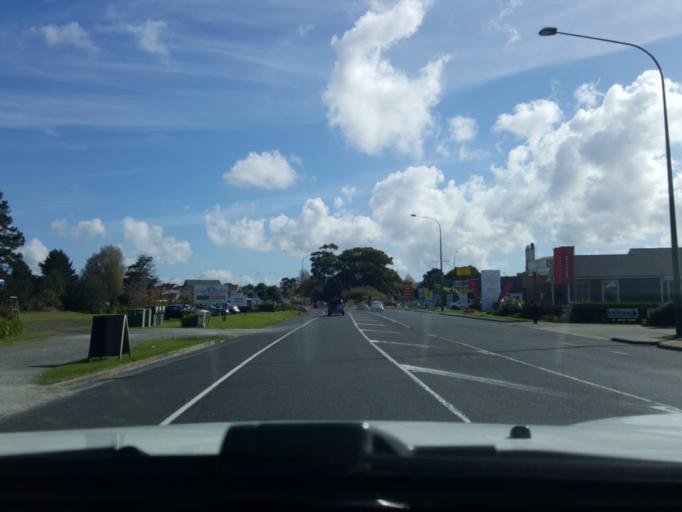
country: NZ
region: Auckland
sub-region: Auckland
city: Muriwai Beach
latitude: -36.7740
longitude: 174.5508
